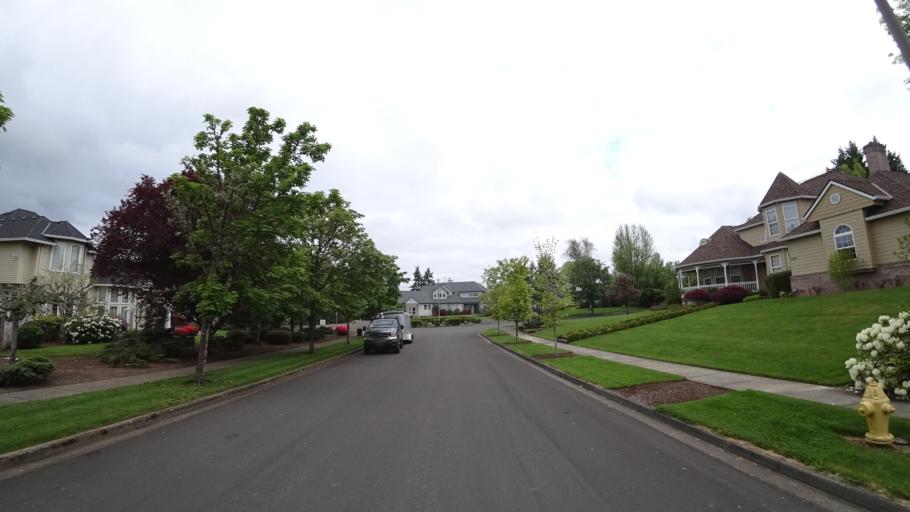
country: US
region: Oregon
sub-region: Washington County
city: Hillsboro
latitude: 45.5486
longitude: -122.9739
